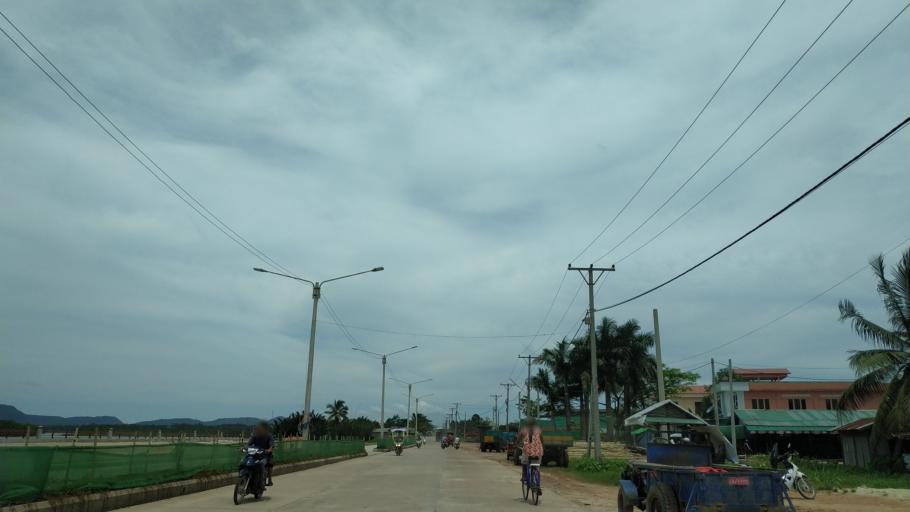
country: MM
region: Tanintharyi
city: Dawei
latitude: 14.0749
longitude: 98.1841
